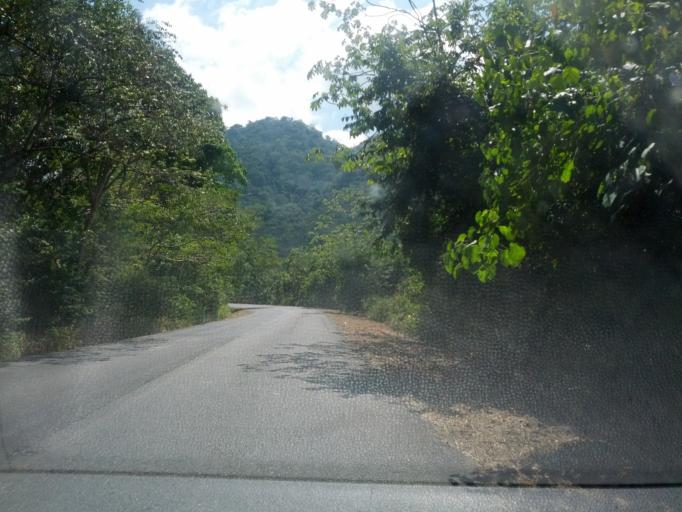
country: CR
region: Puntarenas
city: Ciudad Cortes
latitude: 8.9618
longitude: -83.3133
